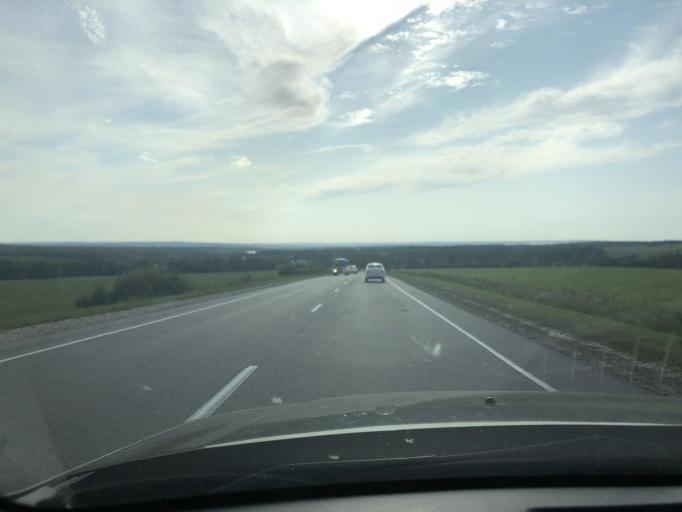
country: RU
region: Tula
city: Krapivna
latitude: 54.1208
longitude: 37.2372
